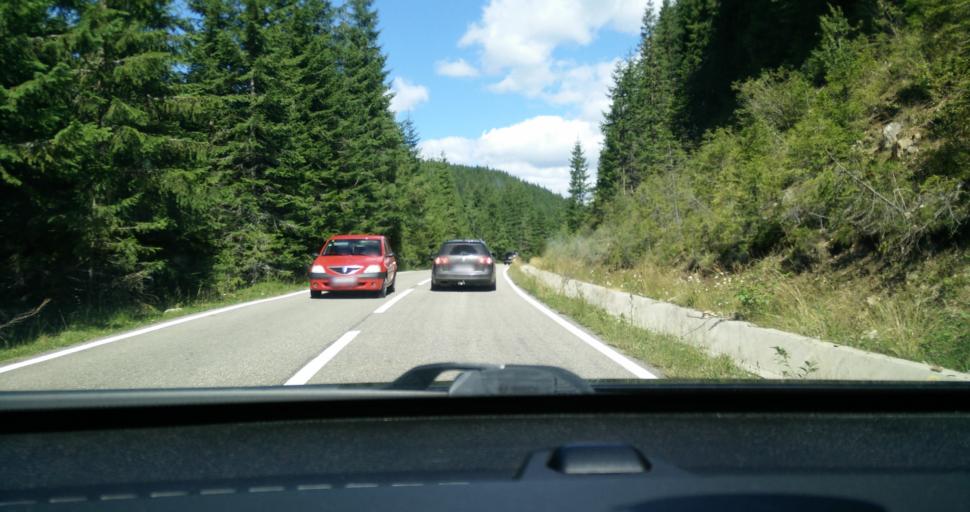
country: RO
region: Alba
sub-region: Comuna Sugag
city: Sugag
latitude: 45.5346
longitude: 23.6404
